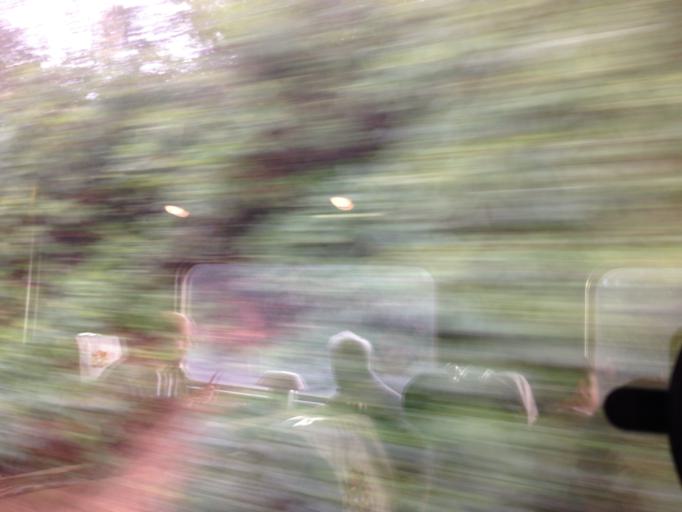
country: GB
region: Scotland
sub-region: Argyll and Bute
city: Garelochhead
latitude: 56.1720
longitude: -4.7778
